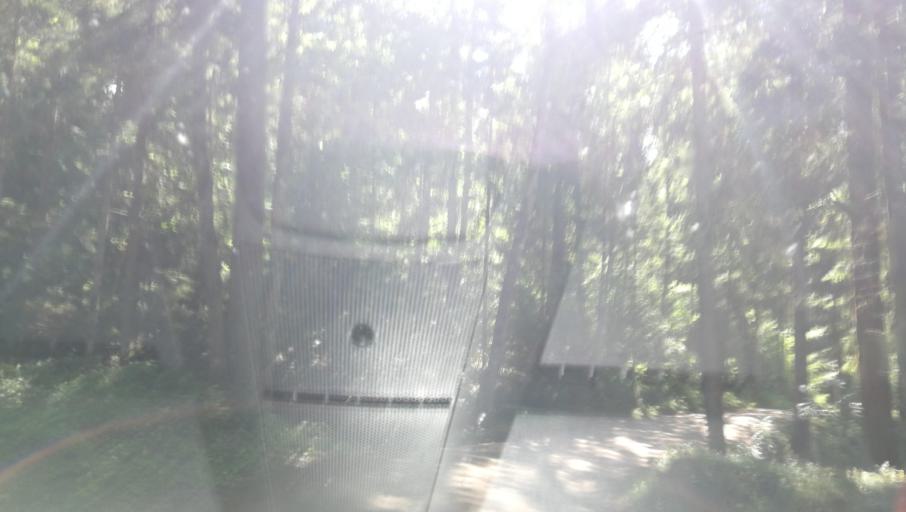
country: LV
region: Cesu Rajons
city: Cesis
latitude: 57.2894
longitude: 25.2129
